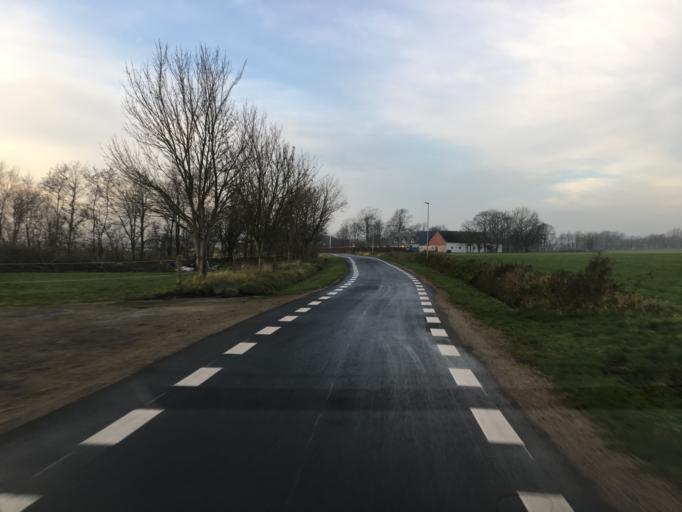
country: DK
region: South Denmark
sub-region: Tonder Kommune
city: Toftlund
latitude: 55.1252
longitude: 9.0684
